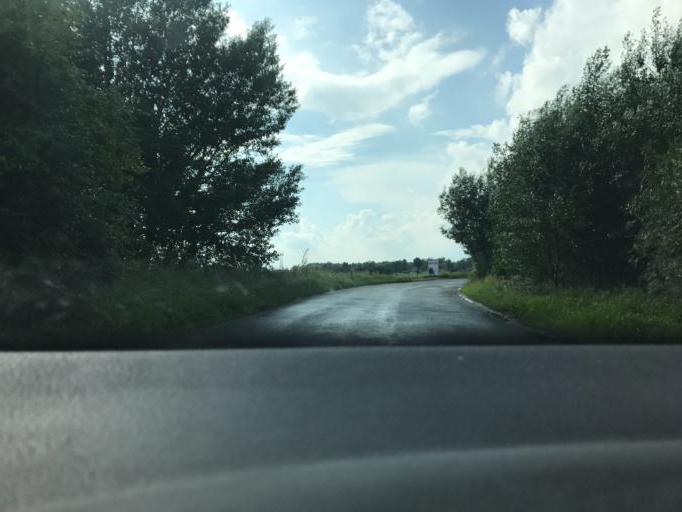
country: PL
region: Pomeranian Voivodeship
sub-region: Powiat gdanski
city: Cedry Wielkie
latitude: 54.3404
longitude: 18.7971
